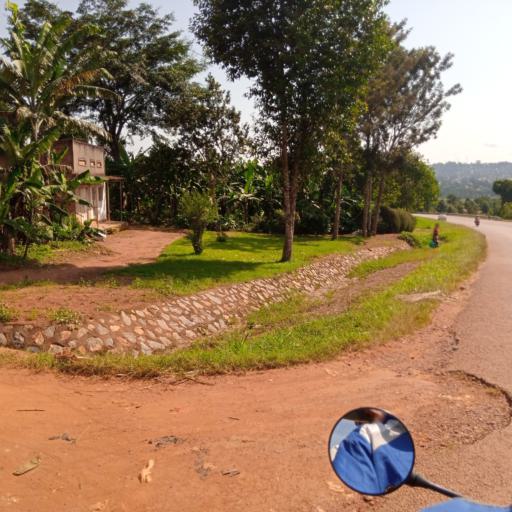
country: UG
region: Central Region
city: Masaka
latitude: -0.3616
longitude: 31.7195
